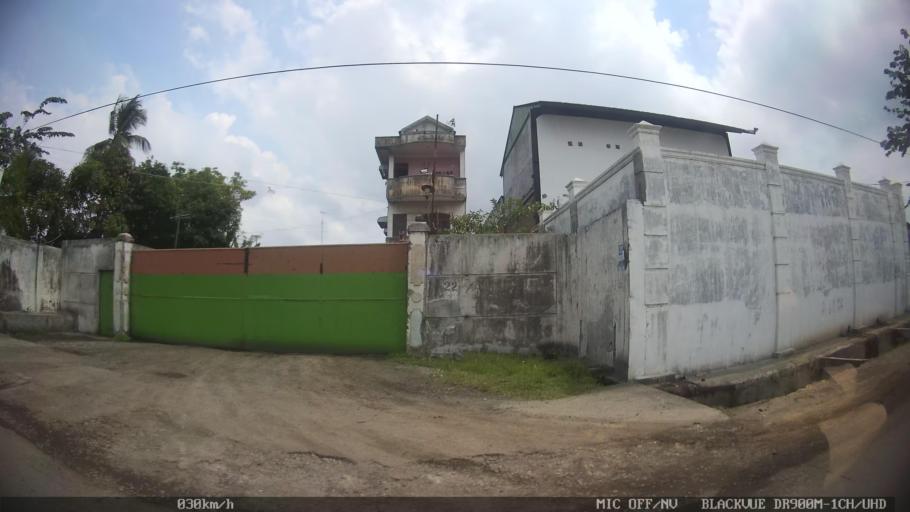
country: ID
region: North Sumatra
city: Medan
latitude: 3.6428
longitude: 98.6728
